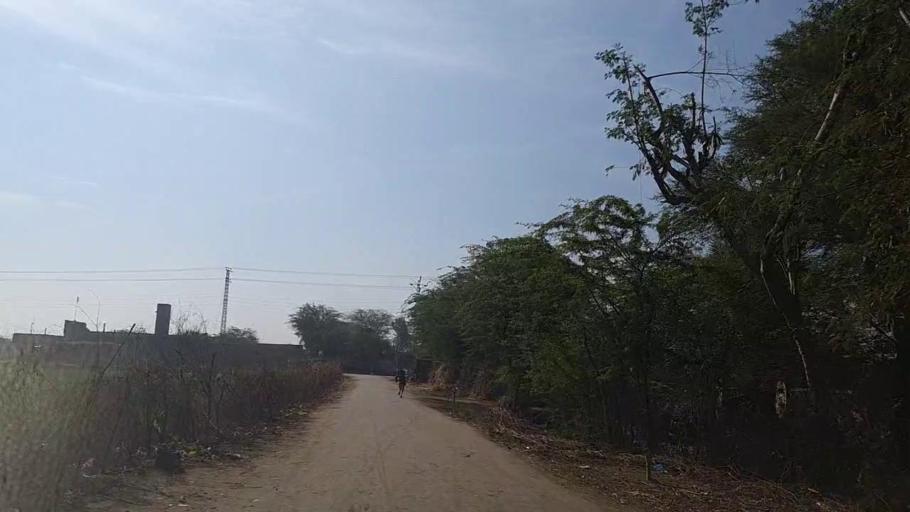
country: PK
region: Sindh
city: Mirpur Khas
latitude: 25.5014
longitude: 69.0022
